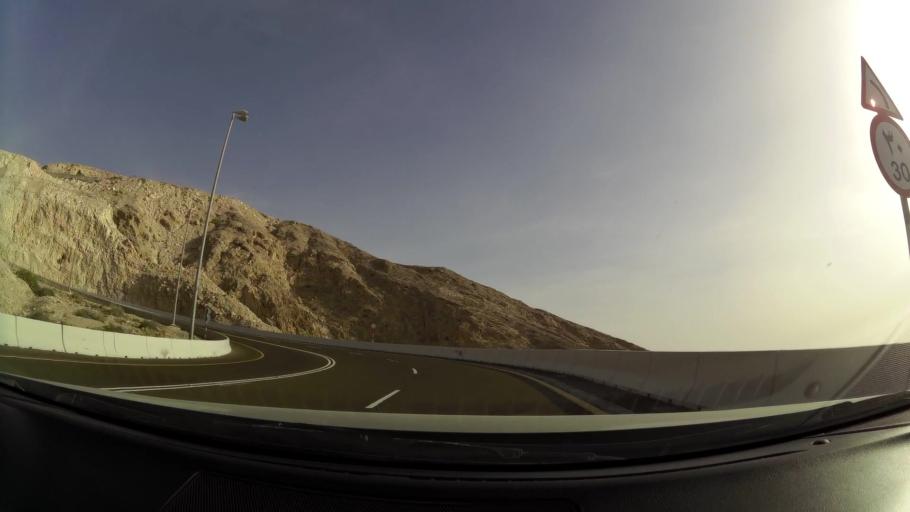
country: AE
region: Abu Dhabi
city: Al Ain
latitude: 24.0873
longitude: 55.7631
